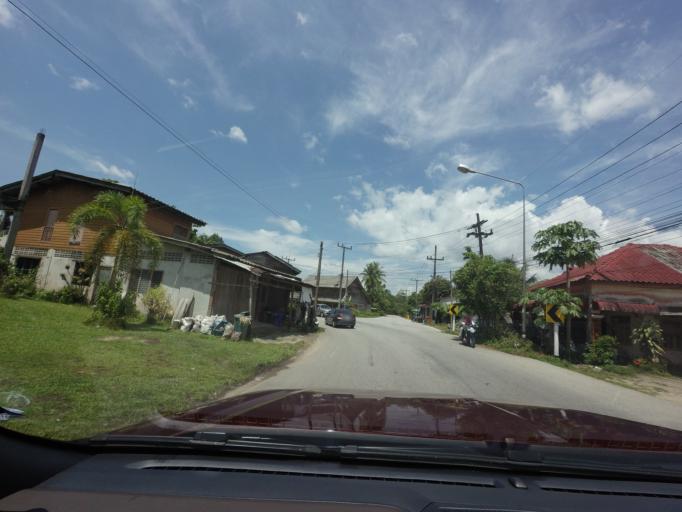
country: TH
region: Narathiwat
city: Ra-ngae
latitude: 6.2302
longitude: 101.6761
